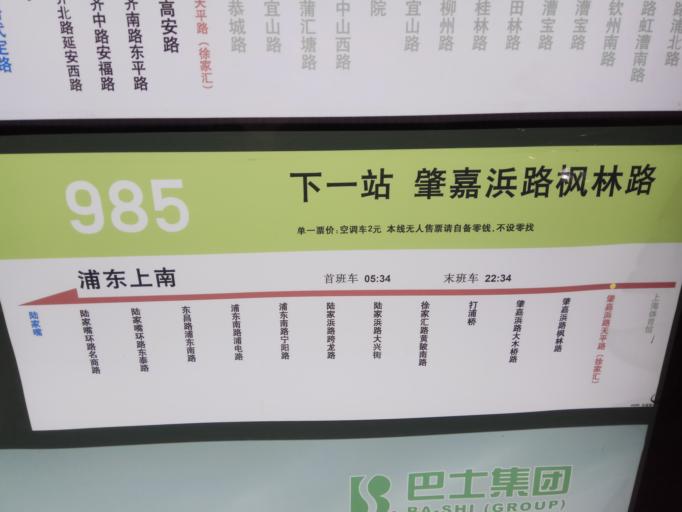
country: CN
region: Shanghai Shi
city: Xuhui
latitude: 31.1972
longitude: 121.4373
